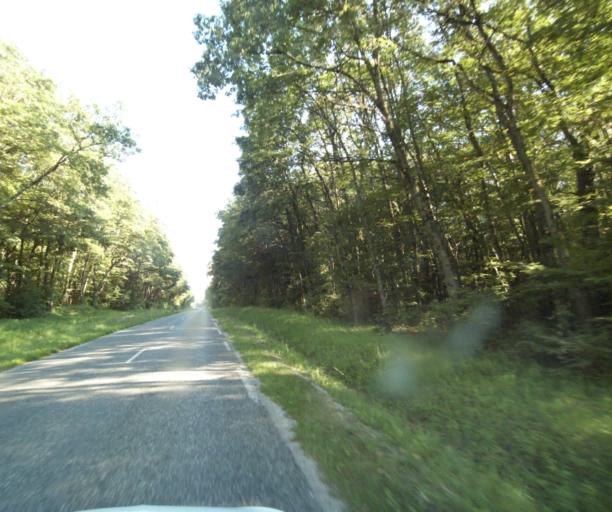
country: FR
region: Rhone-Alpes
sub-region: Departement de la Haute-Savoie
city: Messery
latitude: 46.3295
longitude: 6.2922
